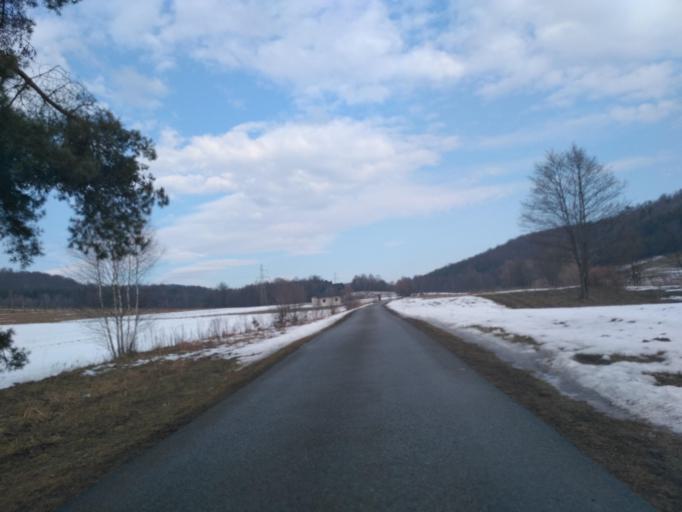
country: PL
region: Subcarpathian Voivodeship
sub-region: Powiat brzozowski
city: Niebocko
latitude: 49.6416
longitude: 22.1295
